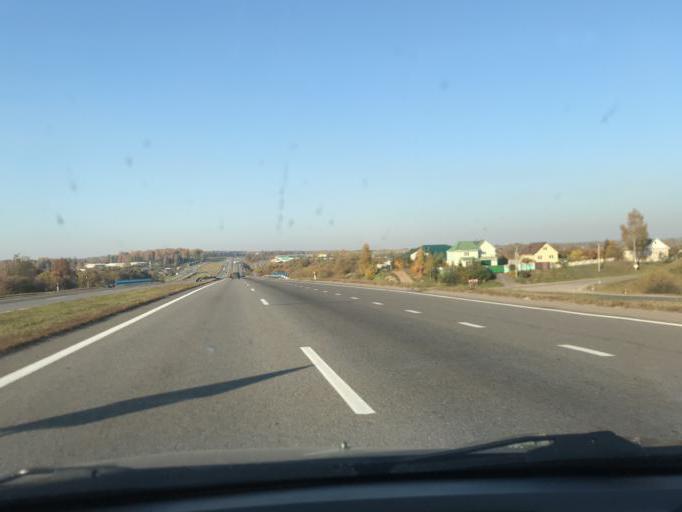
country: BY
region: Minsk
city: Samakhvalavichy
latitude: 53.7377
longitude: 27.5160
